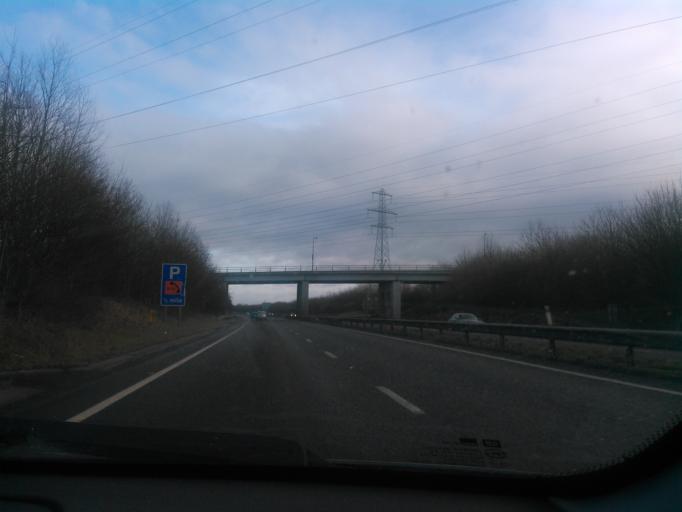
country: GB
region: England
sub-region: Derbyshire
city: Findern
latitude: 52.8662
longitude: -1.5475
